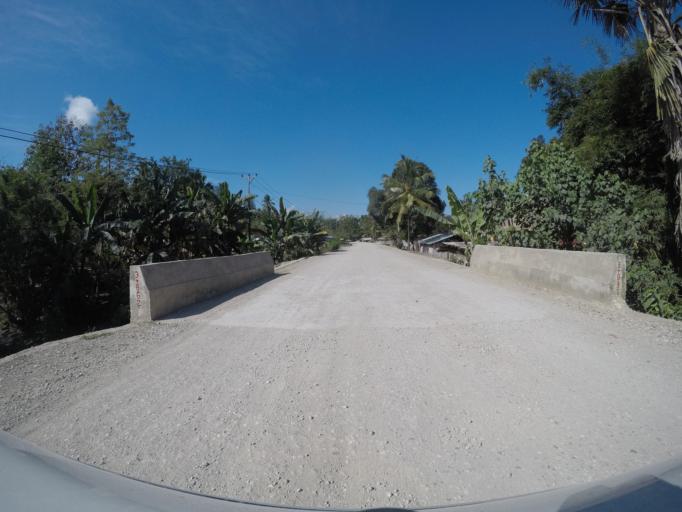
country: TL
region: Viqueque
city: Viqueque
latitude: -8.8432
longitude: 126.5113
